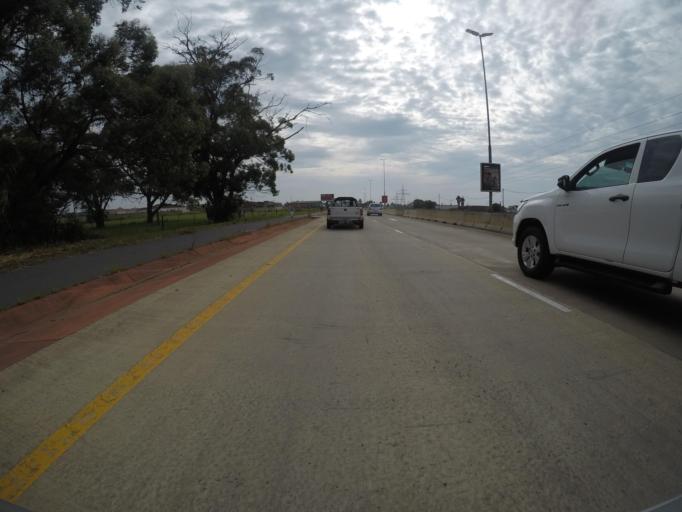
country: ZA
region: Eastern Cape
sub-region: Buffalo City Metropolitan Municipality
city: East London
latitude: -32.9355
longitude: 27.9885
